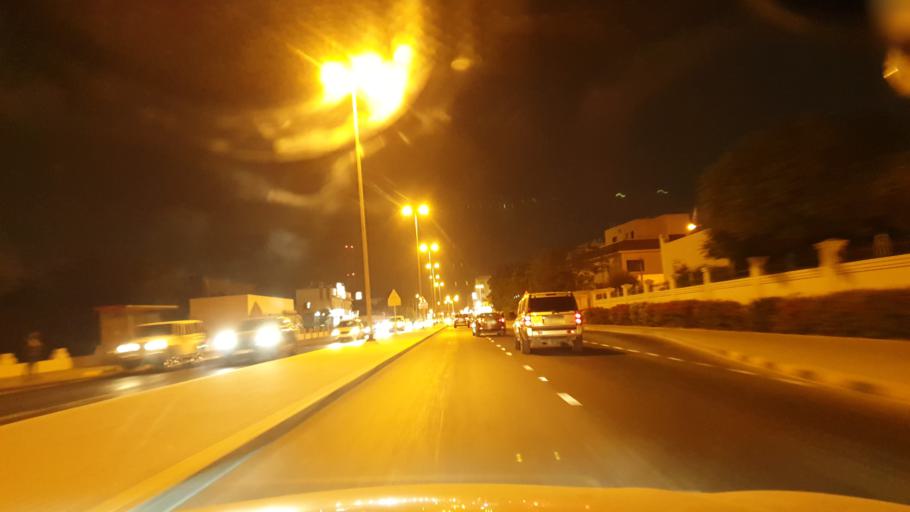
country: BH
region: Manama
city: Jidd Hafs
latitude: 26.1990
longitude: 50.4852
